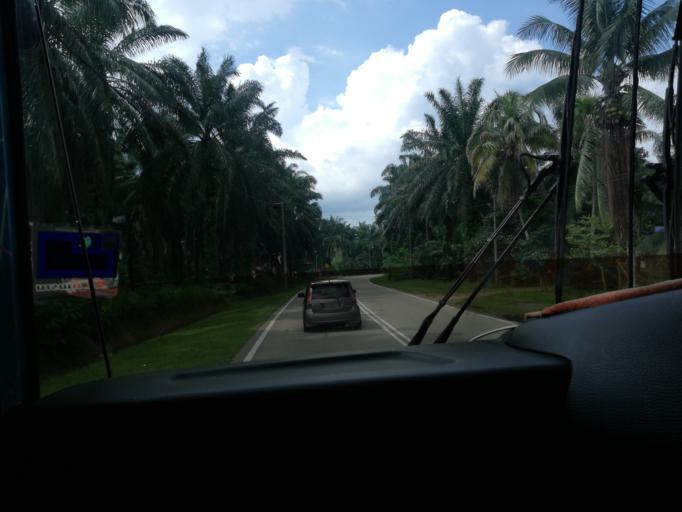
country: MY
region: Kedah
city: Kulim
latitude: 5.2388
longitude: 100.6013
